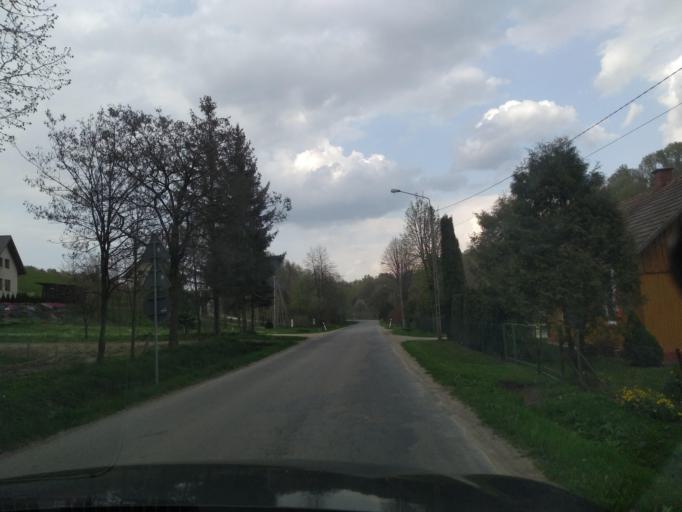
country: PL
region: Subcarpathian Voivodeship
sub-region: Powiat sanocki
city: Czaszyn
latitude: 49.4381
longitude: 22.2508
